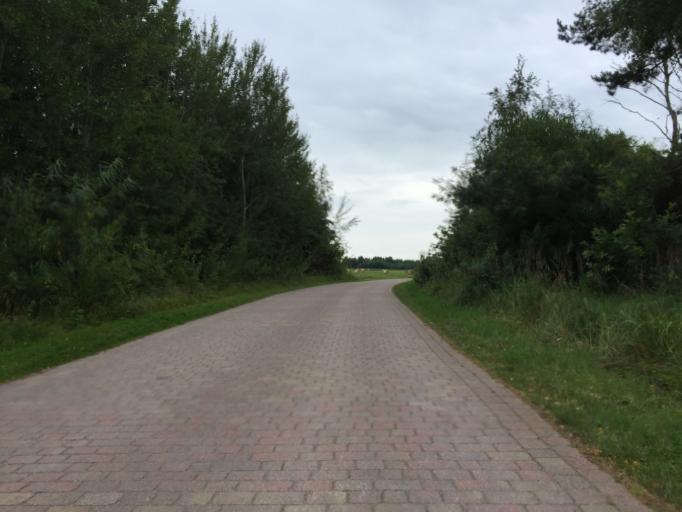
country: DE
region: Mecklenburg-Vorpommern
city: Hiddensee
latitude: 54.5393
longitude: 13.0987
